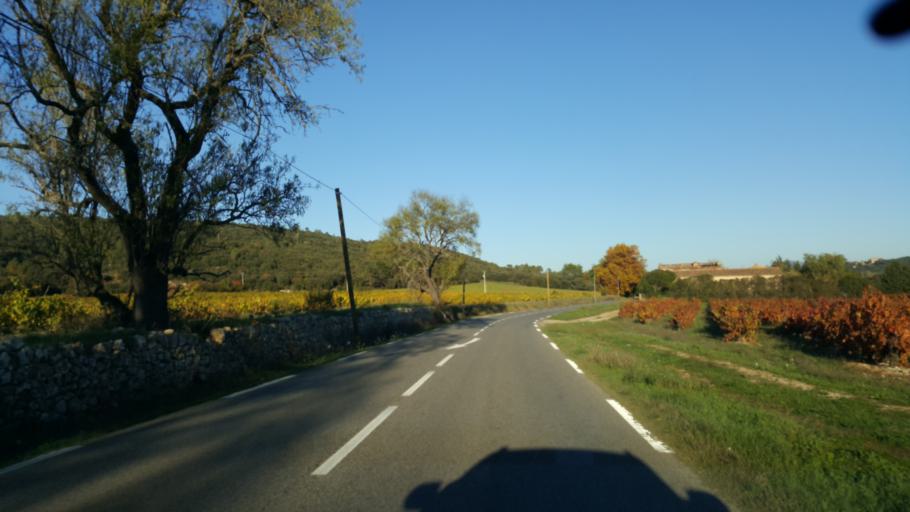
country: FR
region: Provence-Alpes-Cote d'Azur
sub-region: Departement du Var
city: Bras
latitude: 43.5000
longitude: 5.9018
